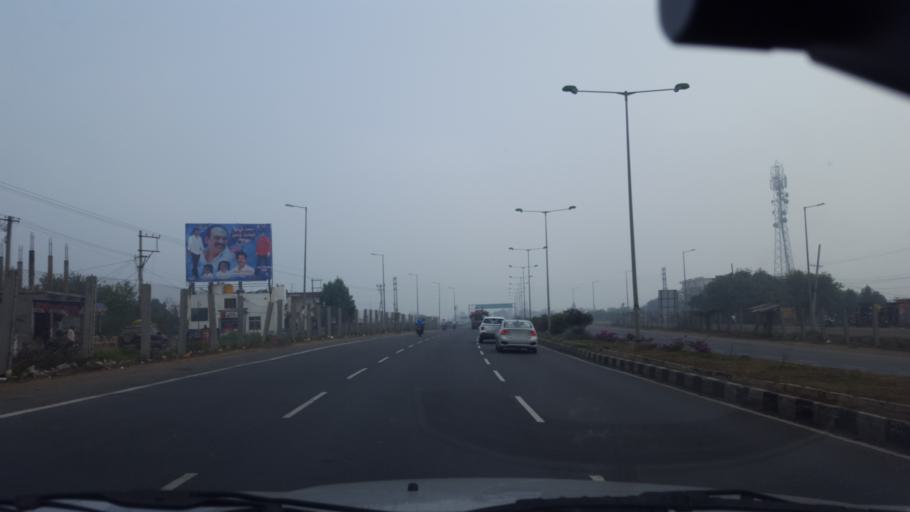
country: IN
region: Andhra Pradesh
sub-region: Prakasam
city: Ongole
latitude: 15.5452
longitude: 80.0529
